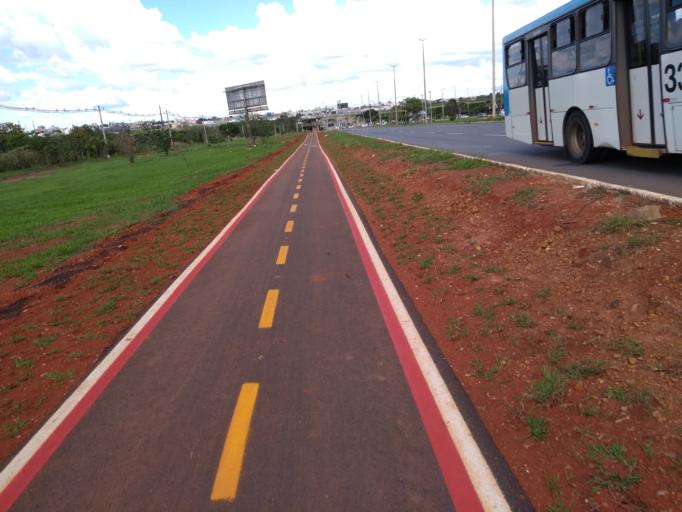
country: BR
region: Federal District
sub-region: Brasilia
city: Brasilia
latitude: -15.8112
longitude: -47.9793
